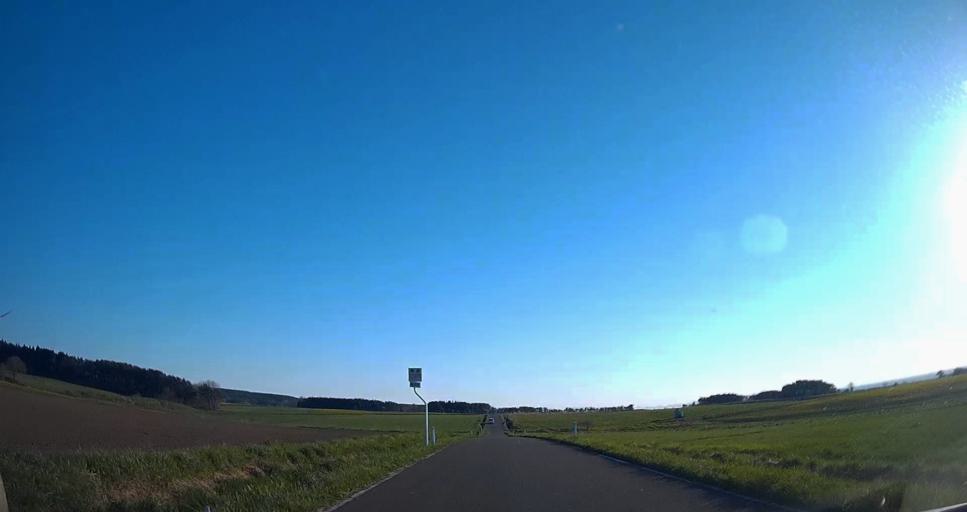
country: JP
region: Aomori
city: Mutsu
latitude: 41.1188
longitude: 141.2771
